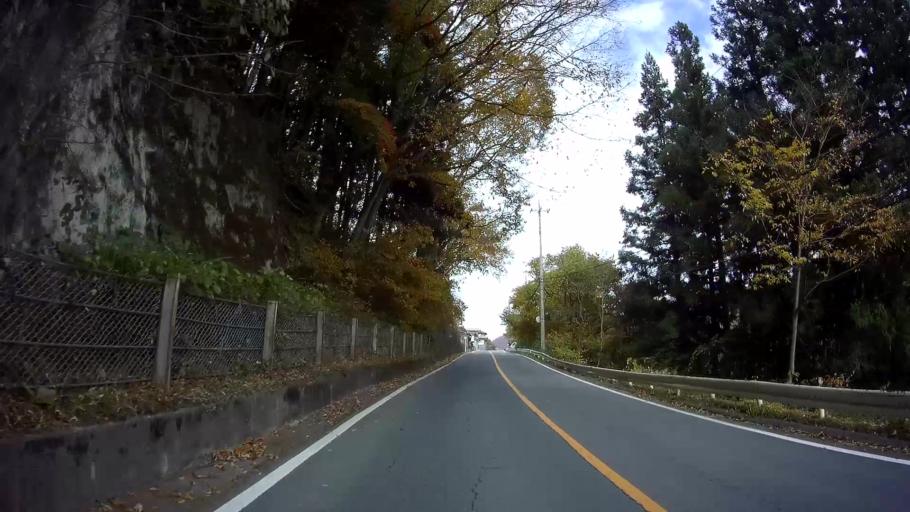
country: JP
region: Gunma
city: Nakanojomachi
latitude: 36.5941
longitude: 138.6260
